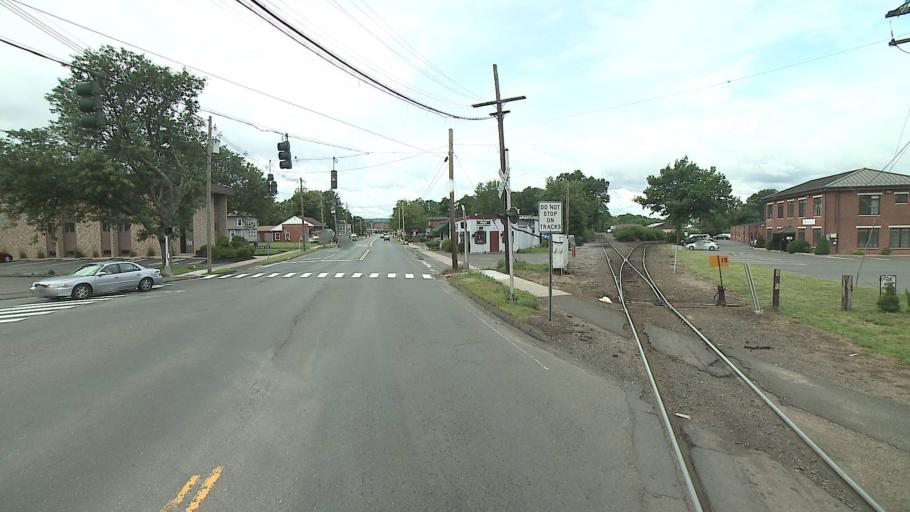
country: US
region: Connecticut
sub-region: Hartford County
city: Plainville
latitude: 41.6732
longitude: -72.8619
